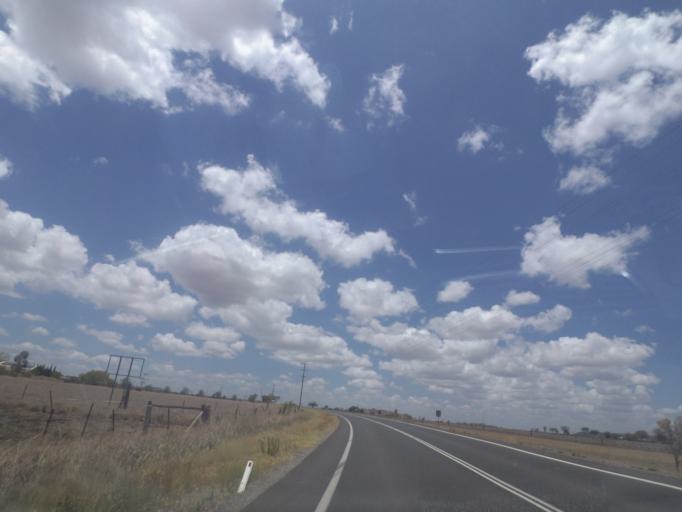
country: AU
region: Queensland
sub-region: Toowoomba
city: Top Camp
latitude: -27.7337
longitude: 151.9131
